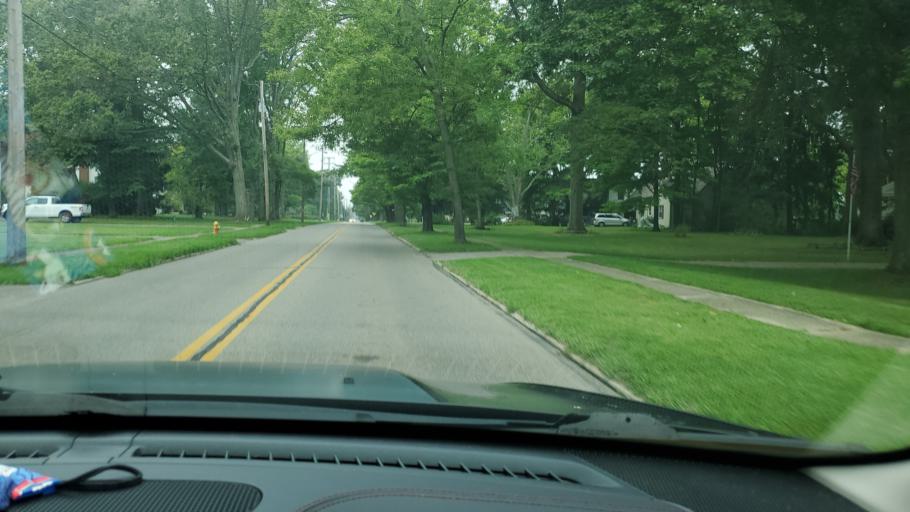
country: US
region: Ohio
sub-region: Mahoning County
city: Boardman
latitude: 41.0464
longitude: -80.6476
